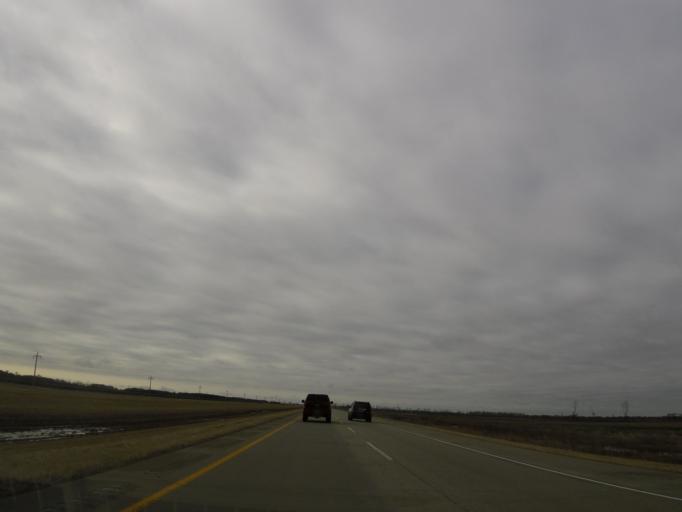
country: US
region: North Dakota
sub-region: Walsh County
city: Grafton
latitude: 48.2617
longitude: -97.1890
